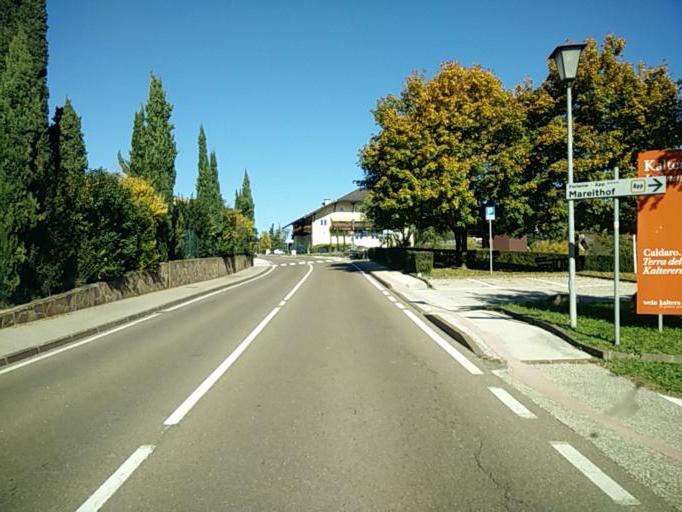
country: IT
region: Trentino-Alto Adige
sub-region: Bolzano
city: Caldaro sulla Strada del Vino
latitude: 46.4141
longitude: 11.2483
